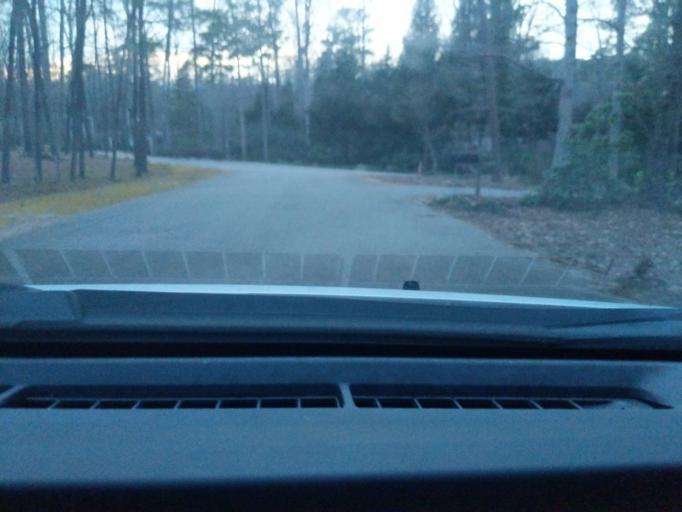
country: US
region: North Carolina
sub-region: Wake County
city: Garner
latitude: 35.7153
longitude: -78.6863
